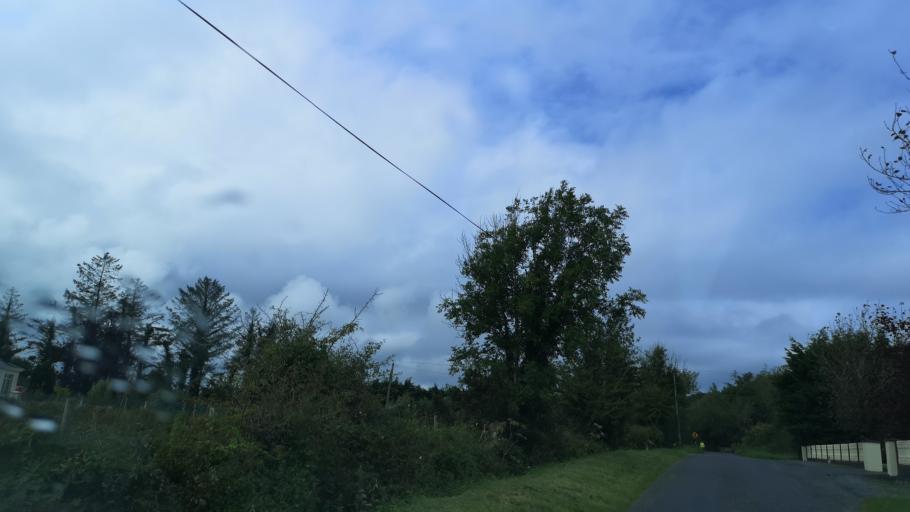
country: IE
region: Connaught
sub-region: County Galway
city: Loughrea
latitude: 53.2980
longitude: -8.5938
